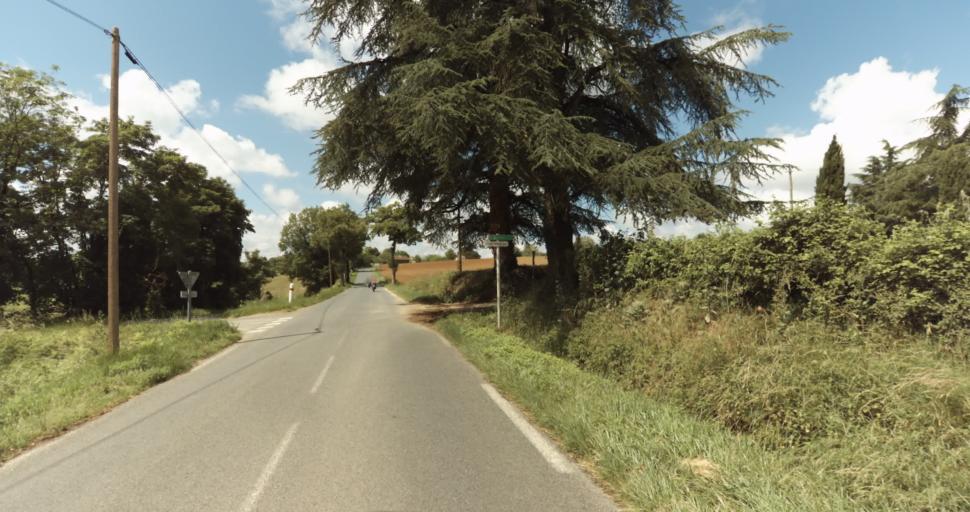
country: FR
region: Aquitaine
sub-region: Departement de la Dordogne
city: Beaumont-du-Perigord
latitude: 44.7786
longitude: 0.8222
